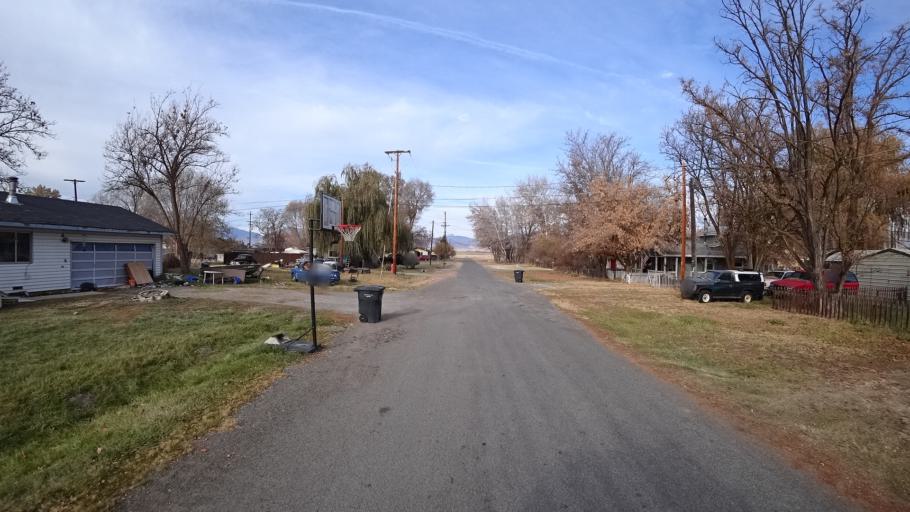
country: US
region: California
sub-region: Siskiyou County
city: Montague
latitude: 41.7322
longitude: -122.5301
